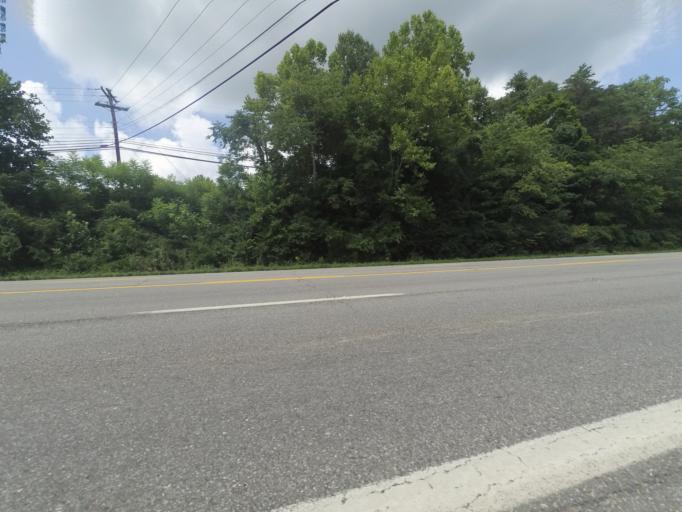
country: US
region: West Virginia
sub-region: Cabell County
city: Pea Ridge
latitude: 38.4103
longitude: -82.3296
